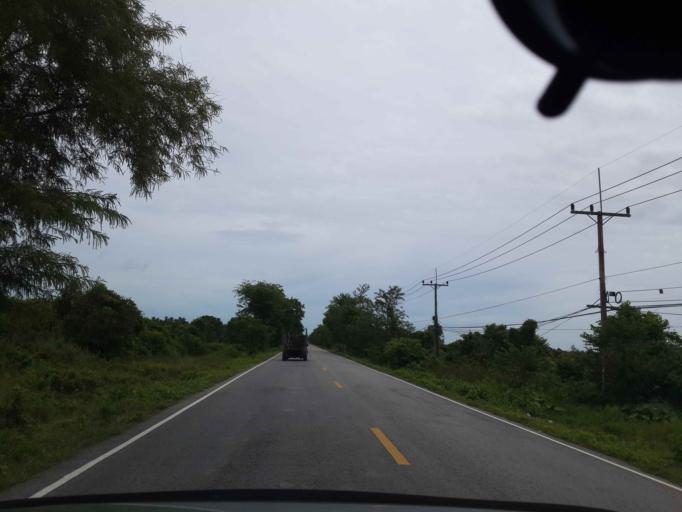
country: TH
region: Narathiwat
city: Yi-ngo
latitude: 6.3868
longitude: 101.6824
